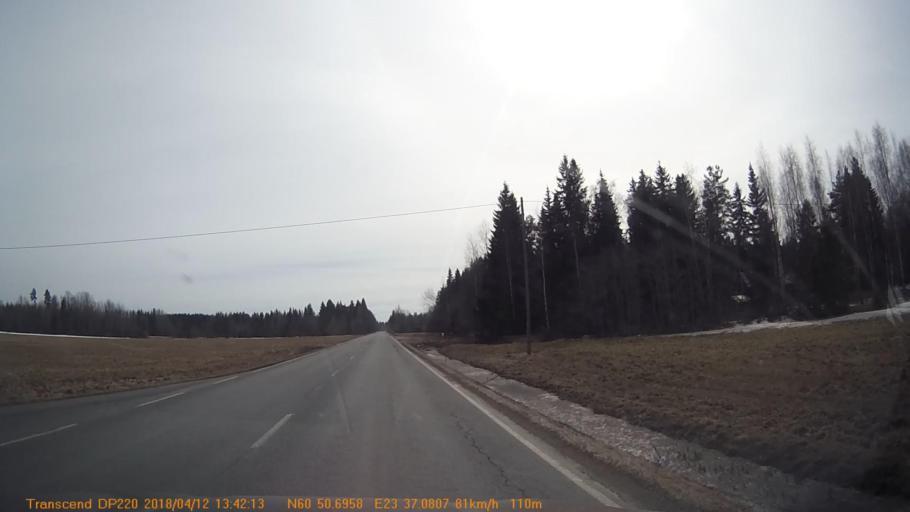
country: FI
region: Haeme
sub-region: Forssa
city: Forssa
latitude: 60.8442
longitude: 23.6180
